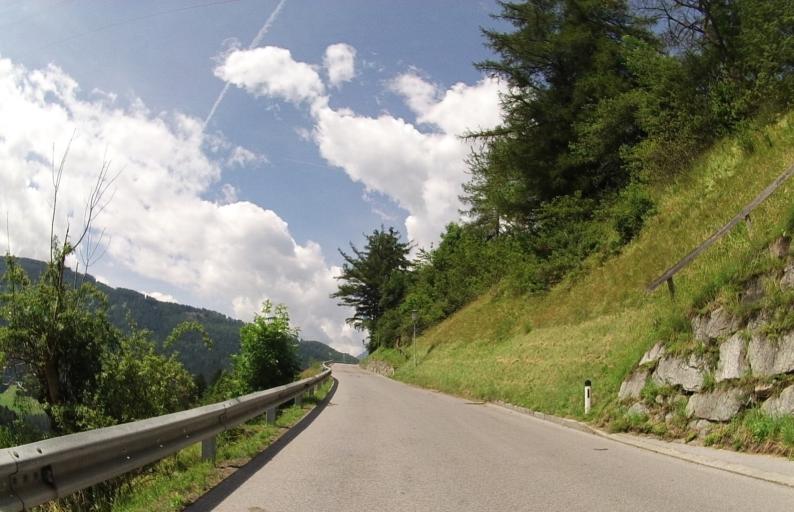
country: AT
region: Tyrol
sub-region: Politischer Bezirk Innsbruck Land
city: Schoenberg im Stubaital
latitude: 47.1856
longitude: 11.4333
